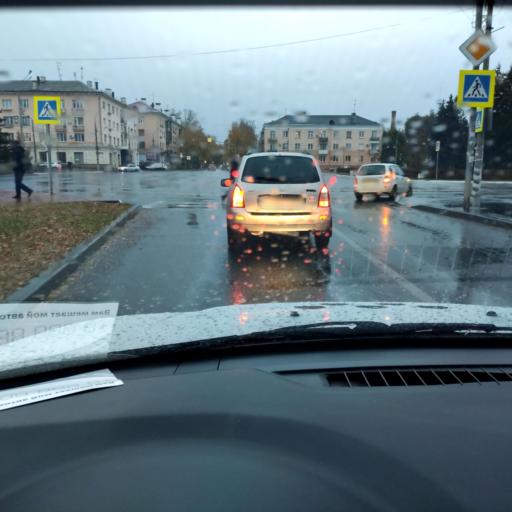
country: RU
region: Samara
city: Tol'yatti
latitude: 53.5145
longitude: 49.4095
